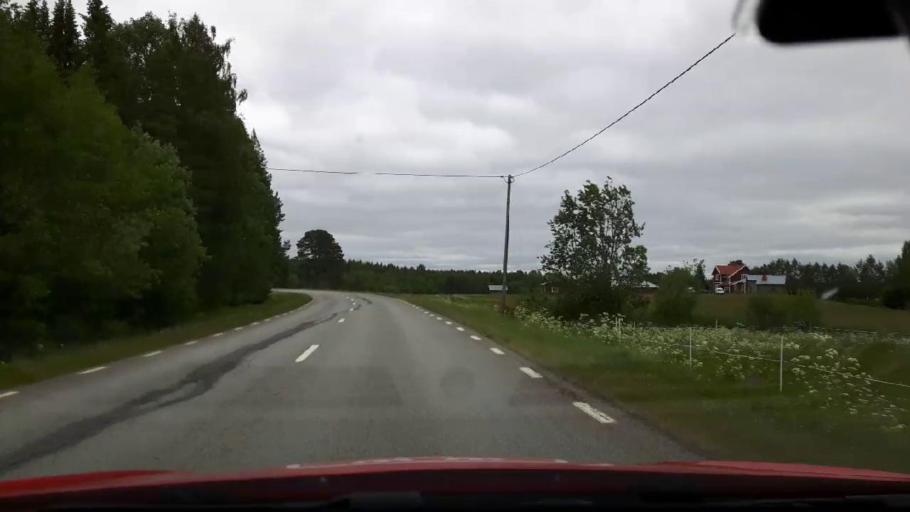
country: SE
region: Jaemtland
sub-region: Stroemsunds Kommun
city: Stroemsund
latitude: 63.5328
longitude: 15.4488
